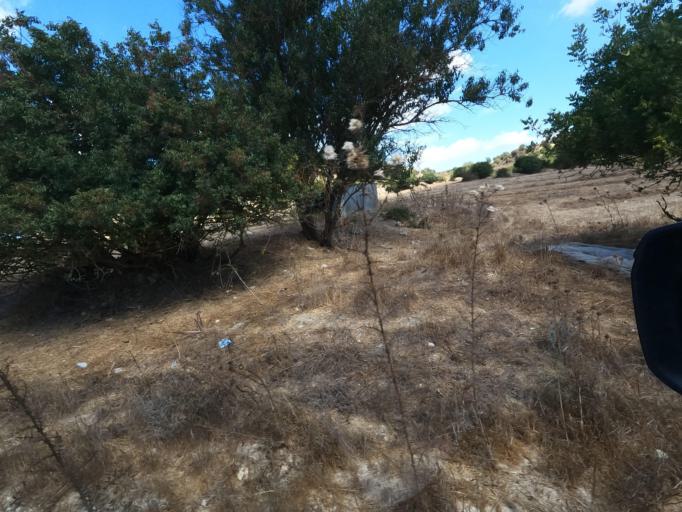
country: CY
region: Pafos
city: Mesogi
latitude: 34.8258
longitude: 32.5511
